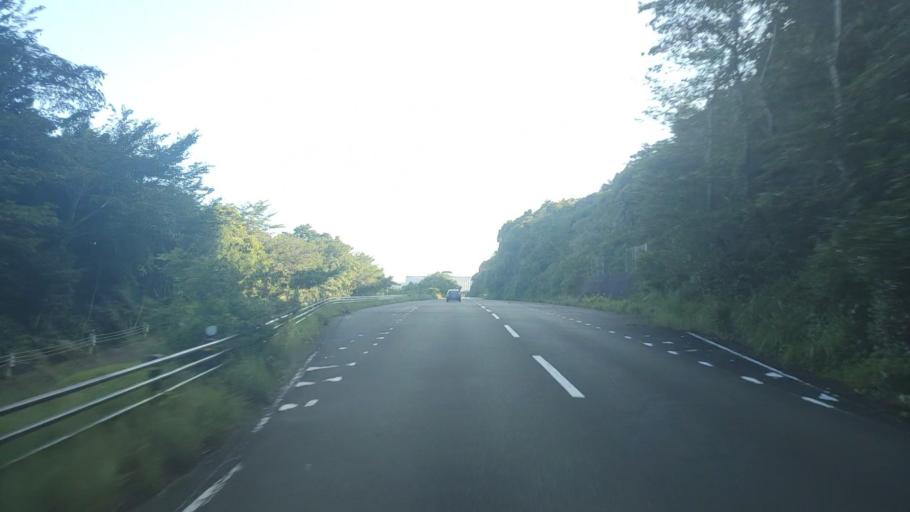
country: JP
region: Mie
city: Toba
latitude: 34.3815
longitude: 136.8577
